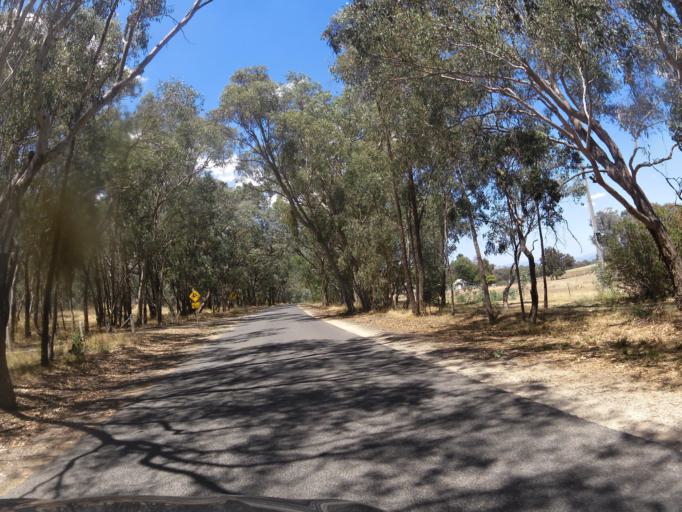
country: AU
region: Victoria
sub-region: Wangaratta
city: Wangaratta
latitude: -36.4065
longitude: 146.5453
